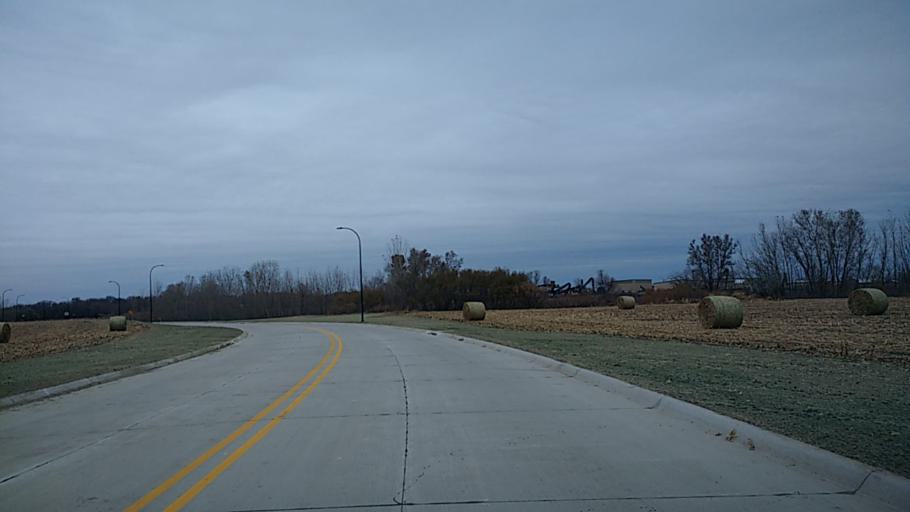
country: US
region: Iowa
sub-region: Woodbury County
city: Sergeant Bluff
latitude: 42.4169
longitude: -96.3724
